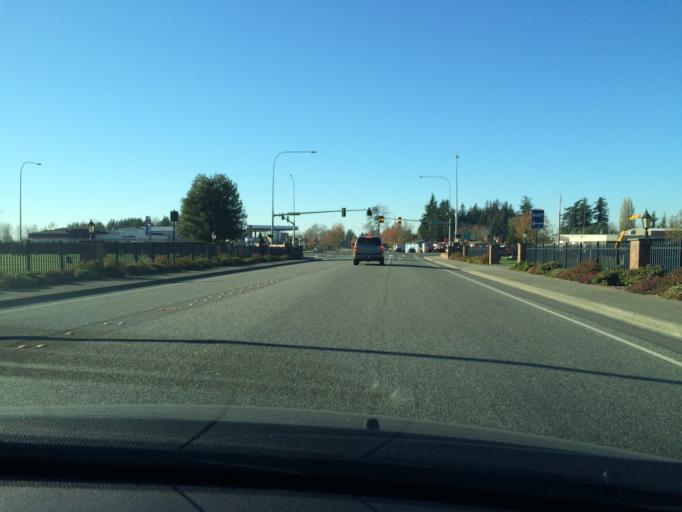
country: US
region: Washington
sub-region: Whatcom County
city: Lynden
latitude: 48.9392
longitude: -122.4840
